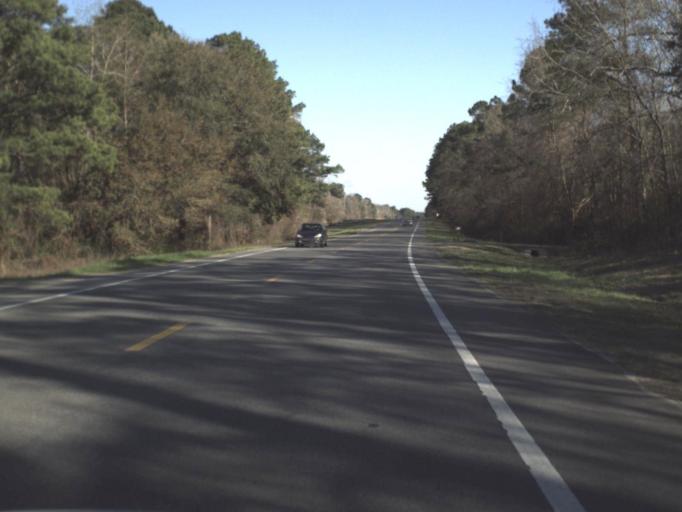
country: US
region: Florida
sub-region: Jackson County
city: Sneads
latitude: 30.7178
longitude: -84.9609
